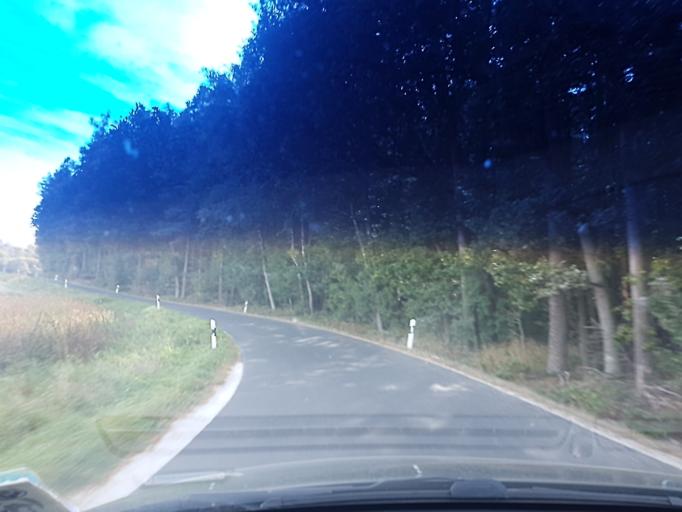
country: DE
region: Bavaria
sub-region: Regierungsbezirk Mittelfranken
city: Wachenroth
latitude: 49.7671
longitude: 10.7157
